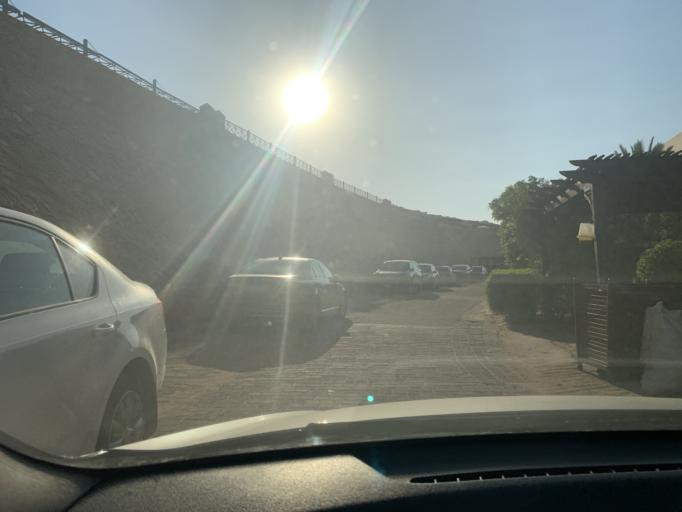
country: EG
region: As Suways
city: Ain Sukhna
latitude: 29.3741
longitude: 32.5716
